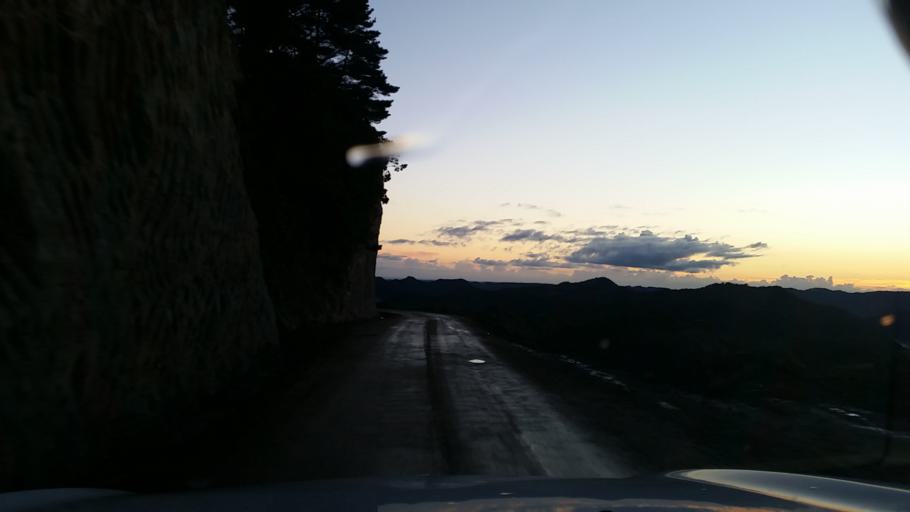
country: NZ
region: Manawatu-Wanganui
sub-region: Wanganui District
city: Wanganui
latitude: -39.7630
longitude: 174.8778
